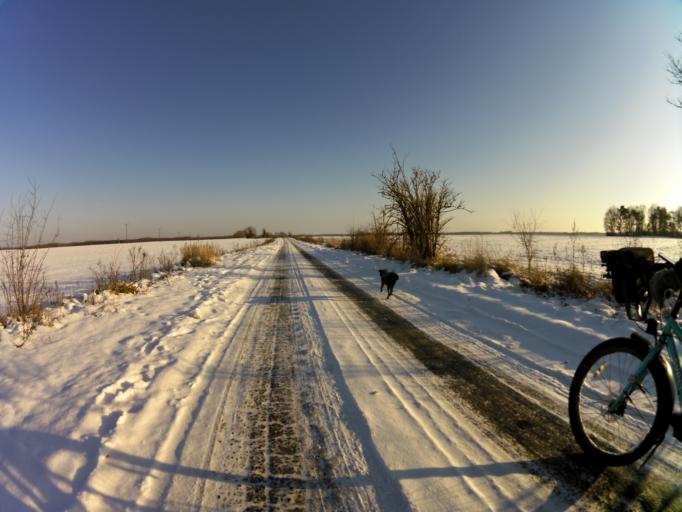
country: PL
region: West Pomeranian Voivodeship
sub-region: Powiat stargardzki
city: Dobrzany
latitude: 53.3322
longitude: 15.4049
